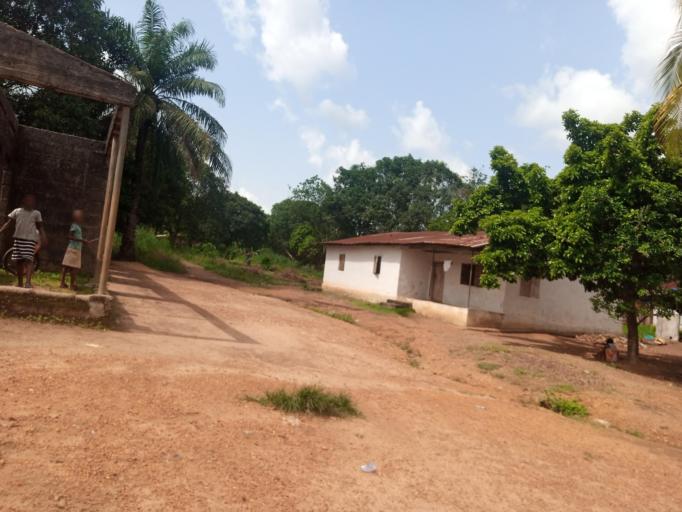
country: SL
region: Southern Province
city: Bo
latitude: 7.9801
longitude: -11.7280
